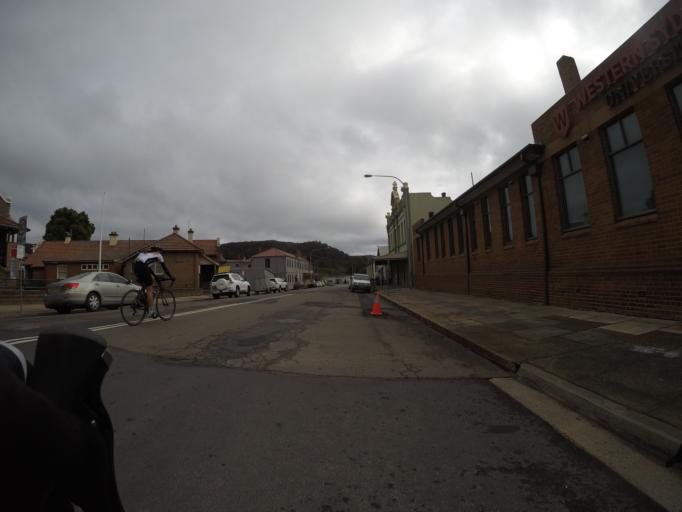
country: AU
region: New South Wales
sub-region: Lithgow
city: Lithgow
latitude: -33.4809
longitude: 150.1615
